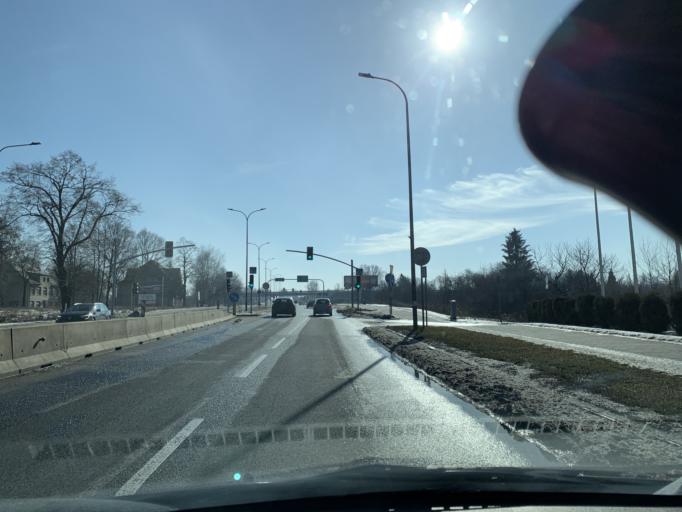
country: PL
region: Silesian Voivodeship
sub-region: Powiat tarnogorski
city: Radzionkow
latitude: 50.3709
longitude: 18.8946
